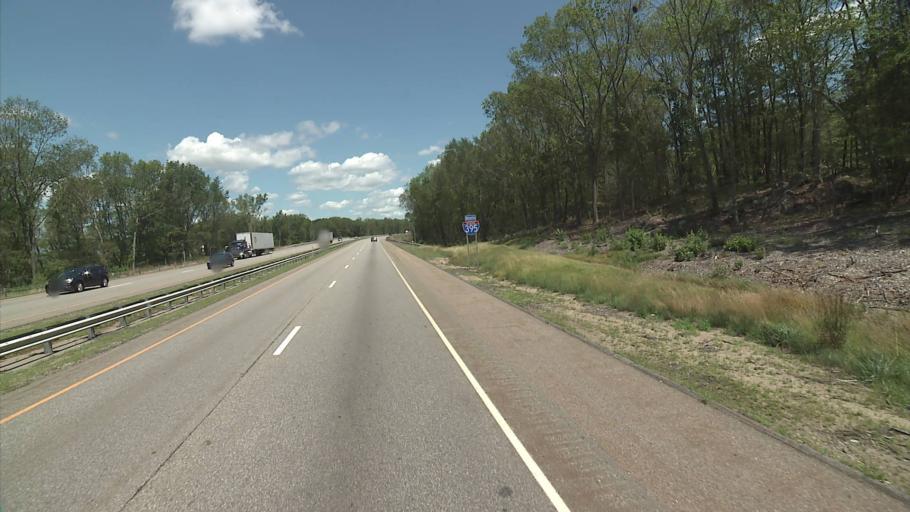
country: US
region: Connecticut
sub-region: New London County
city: Jewett City
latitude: 41.6190
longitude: -71.9447
